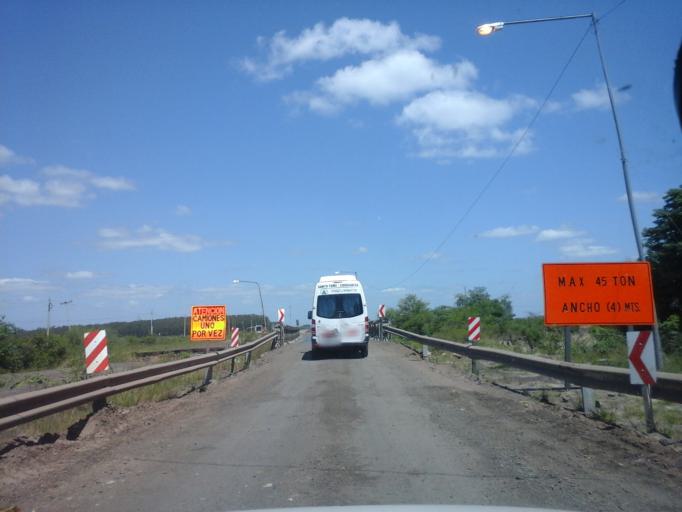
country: AR
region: Corrientes
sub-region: Departamento de Itati
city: Itati
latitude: -27.3296
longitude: -57.9636
